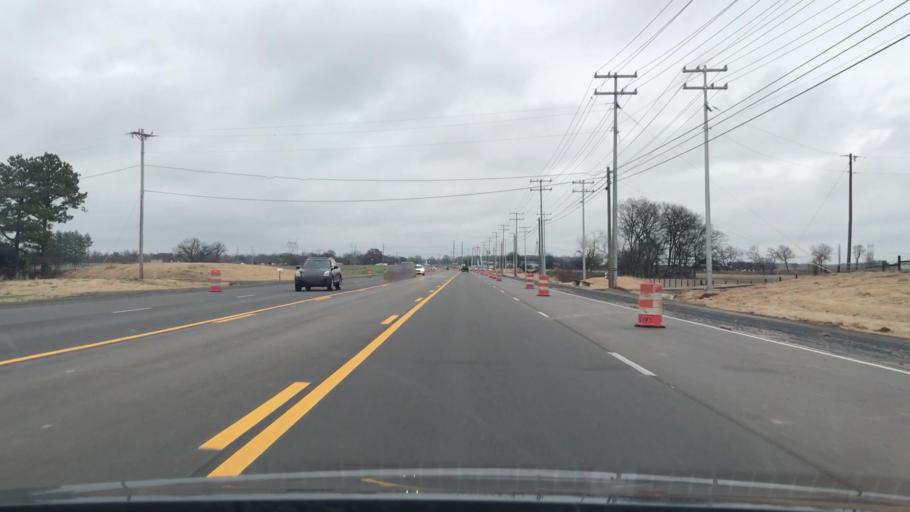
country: US
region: Kentucky
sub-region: Todd County
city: Guthrie
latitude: 36.6084
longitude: -87.2669
